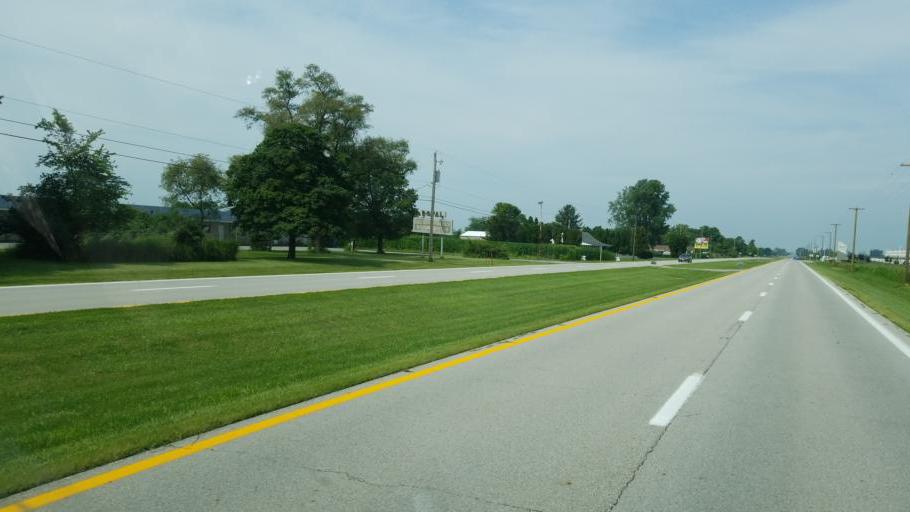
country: US
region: Ohio
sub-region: Madison County
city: West Jefferson
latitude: 39.9421
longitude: -83.3194
